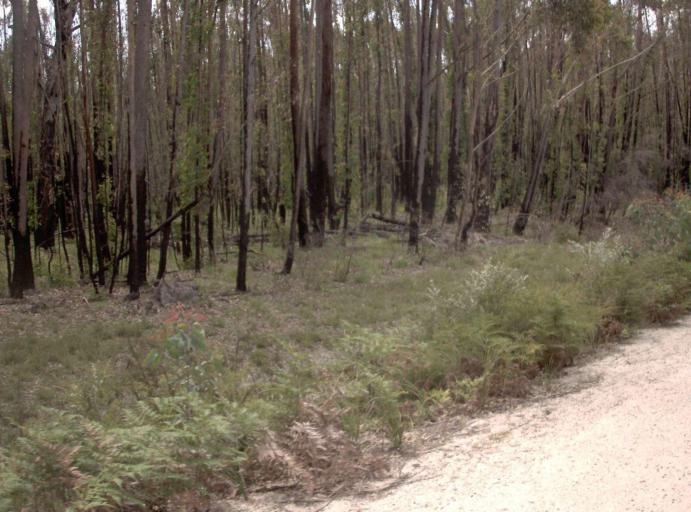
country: AU
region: New South Wales
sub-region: Bega Valley
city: Eden
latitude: -37.5313
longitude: 149.4863
